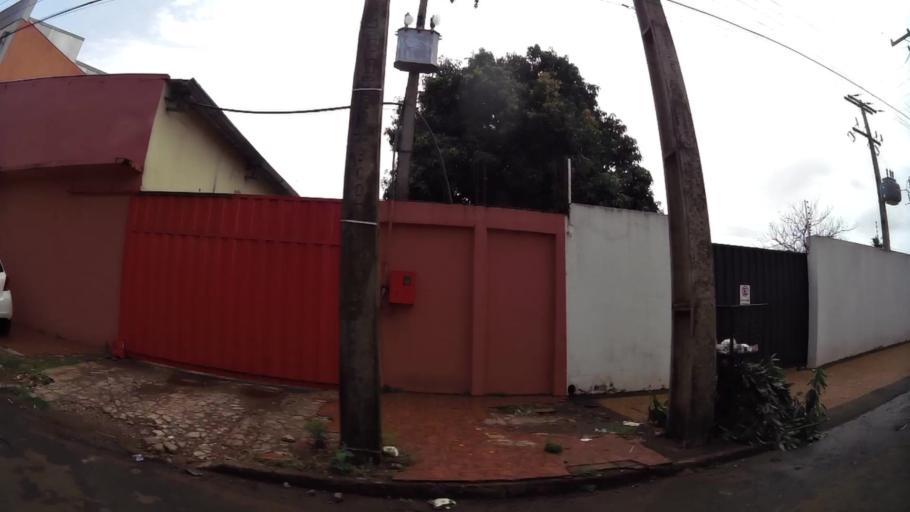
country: PY
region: Alto Parana
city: Ciudad del Este
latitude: -25.4992
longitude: -54.6654
